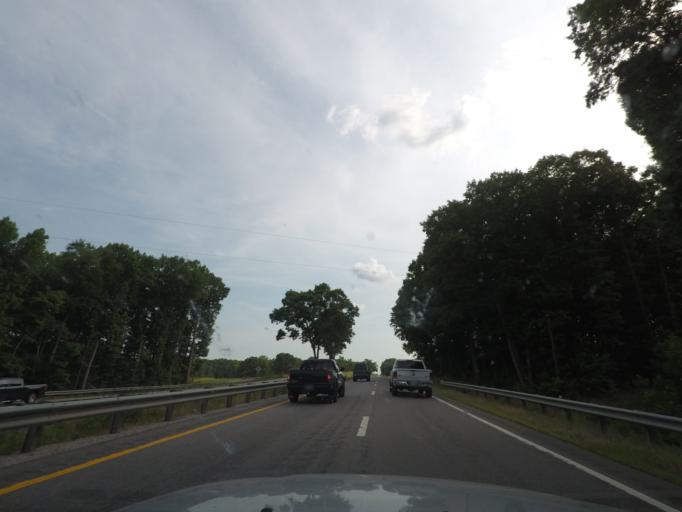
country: US
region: Virginia
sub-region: Mecklenburg County
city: Chase City
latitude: 36.8993
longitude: -78.5398
